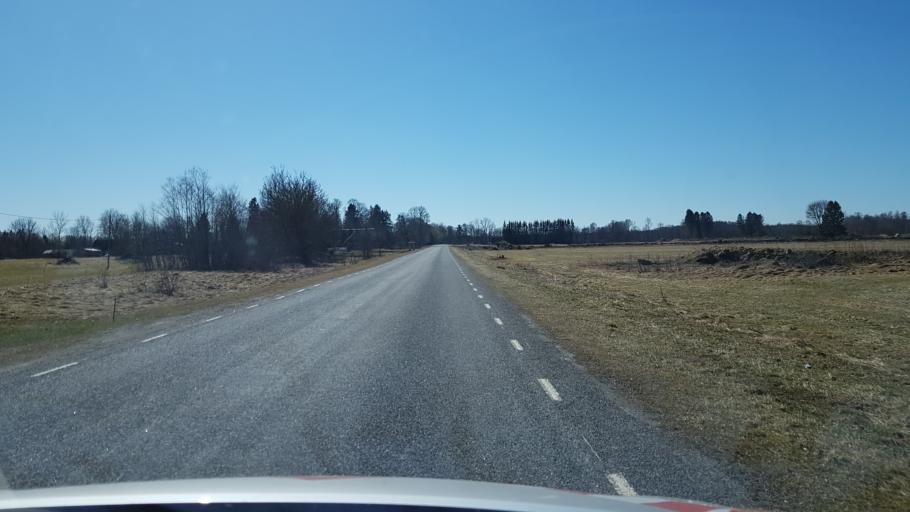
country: EE
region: Laeaene-Virumaa
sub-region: Haljala vald
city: Haljala
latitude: 59.5320
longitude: 26.2360
